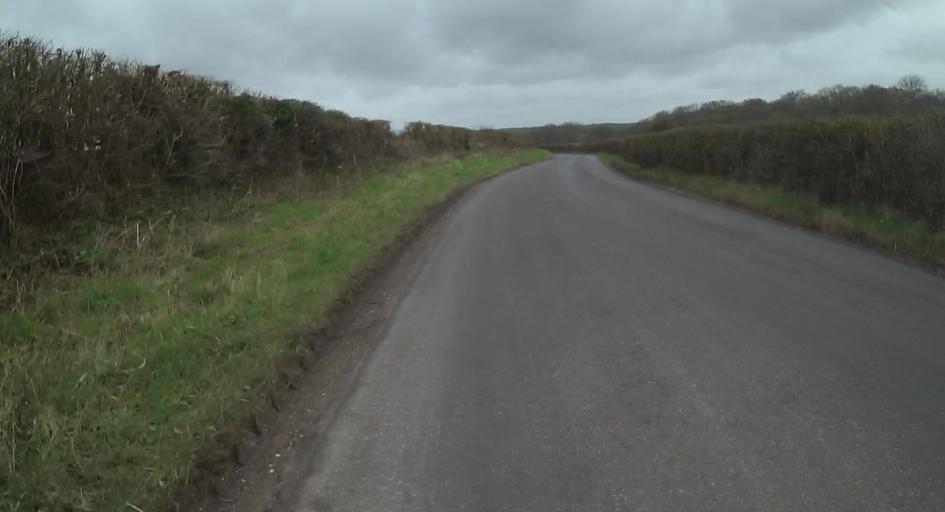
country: GB
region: England
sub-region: Hampshire
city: Kingsclere
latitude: 51.3283
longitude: -1.2732
